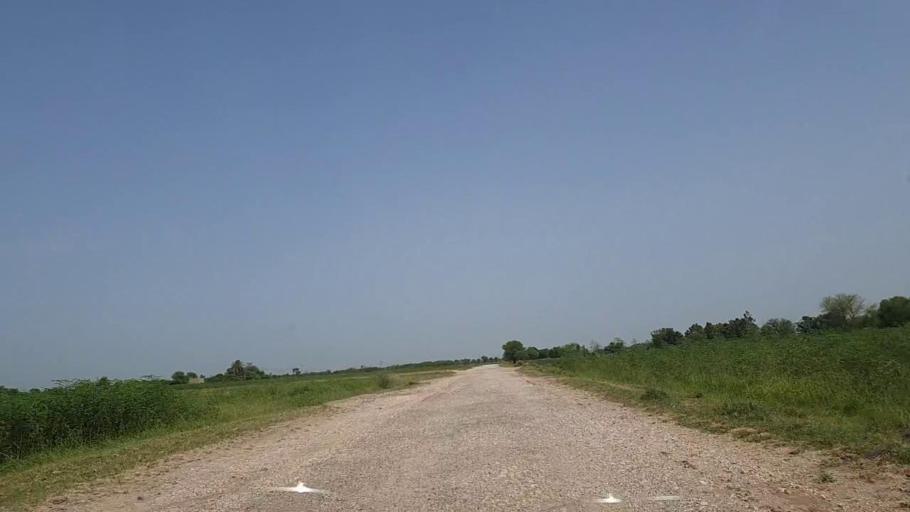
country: PK
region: Sindh
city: Kandiaro
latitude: 27.0143
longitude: 68.1690
